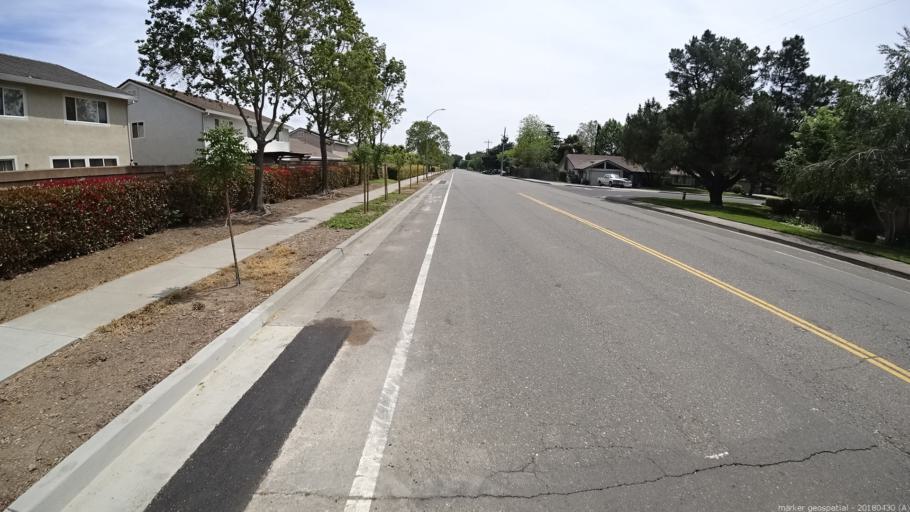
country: US
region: California
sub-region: Yolo County
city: West Sacramento
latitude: 38.5451
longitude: -121.5273
